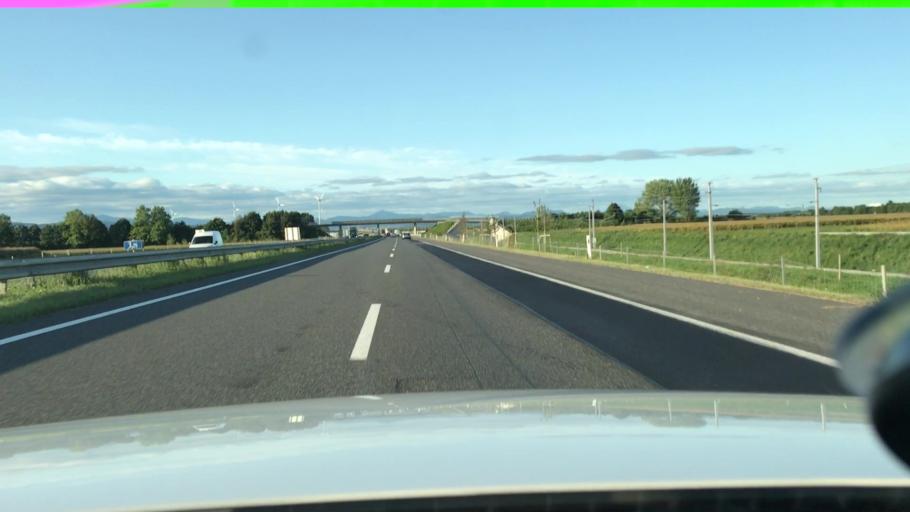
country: AT
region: Lower Austria
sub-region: Sankt Polten Stadt
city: Sankt Poelten
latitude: 48.2084
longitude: 15.6673
